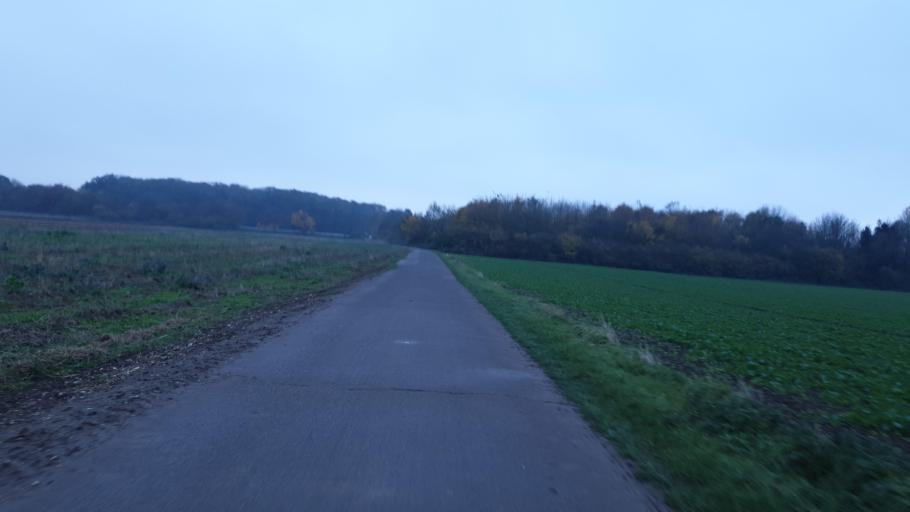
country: DE
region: North Rhine-Westphalia
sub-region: Regierungsbezirk Koln
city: Kerpen
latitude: 50.9176
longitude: 6.6946
